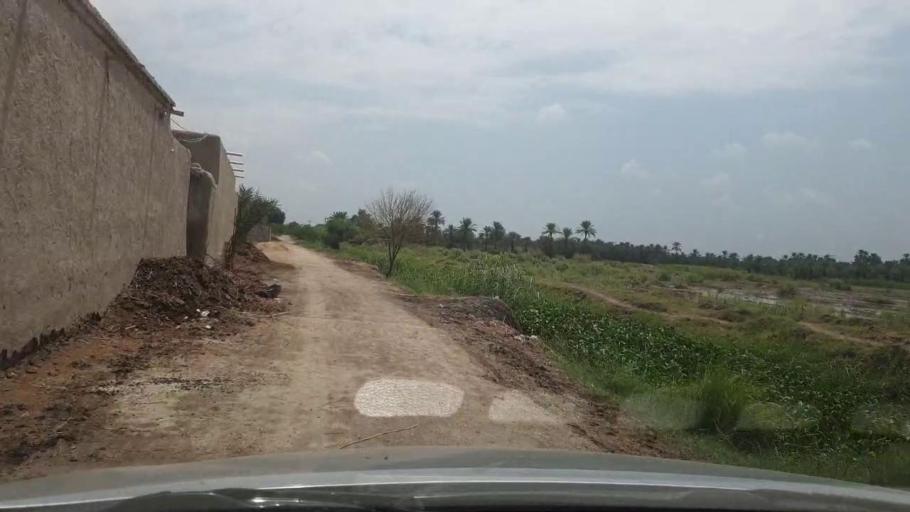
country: PK
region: Sindh
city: Kot Diji
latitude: 27.4212
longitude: 68.7598
